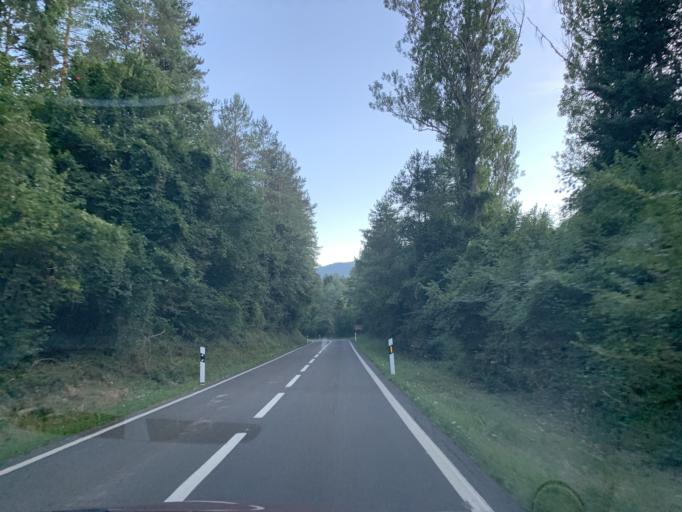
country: ES
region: Aragon
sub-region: Provincia de Huesca
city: Broto
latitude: 42.5632
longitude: -0.1158
